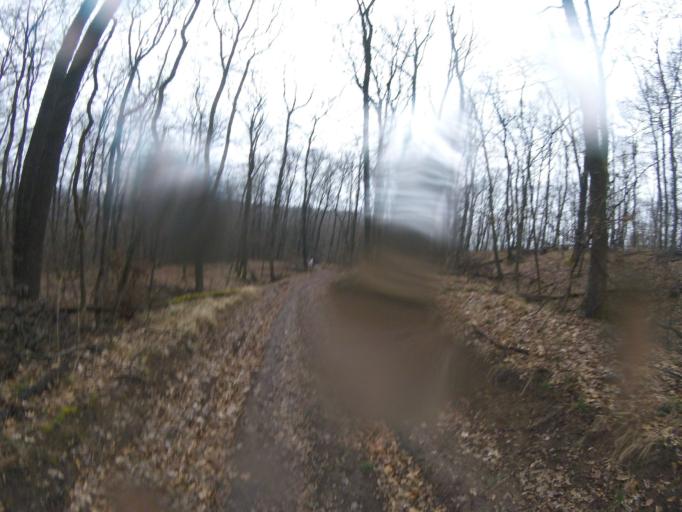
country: HU
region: Pest
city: Szob
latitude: 47.8059
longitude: 18.8227
